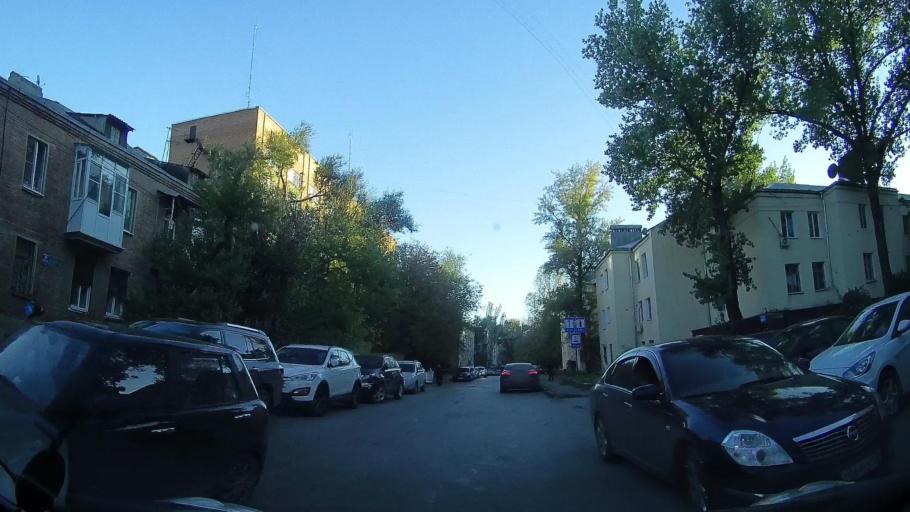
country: RU
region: Rostov
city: Rostov-na-Donu
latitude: 47.2389
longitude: 39.7025
